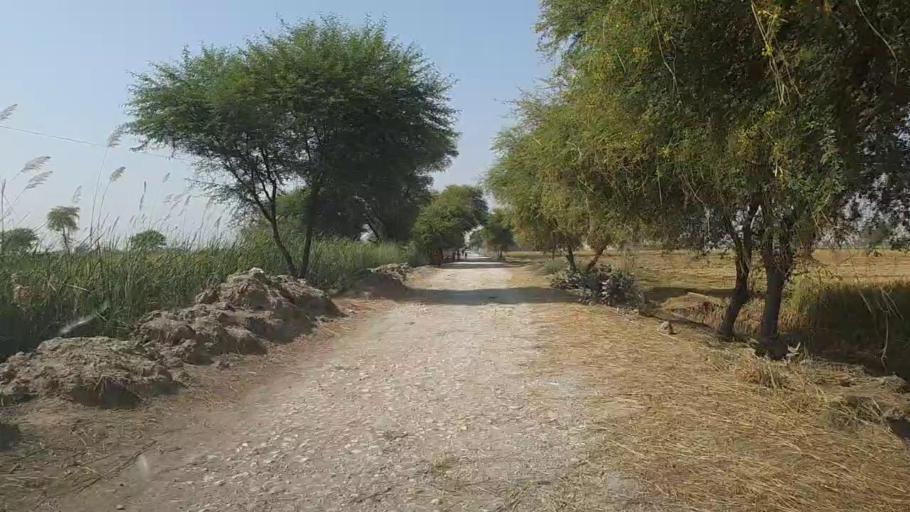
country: PK
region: Sindh
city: Kandhkot
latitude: 28.3950
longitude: 69.2965
